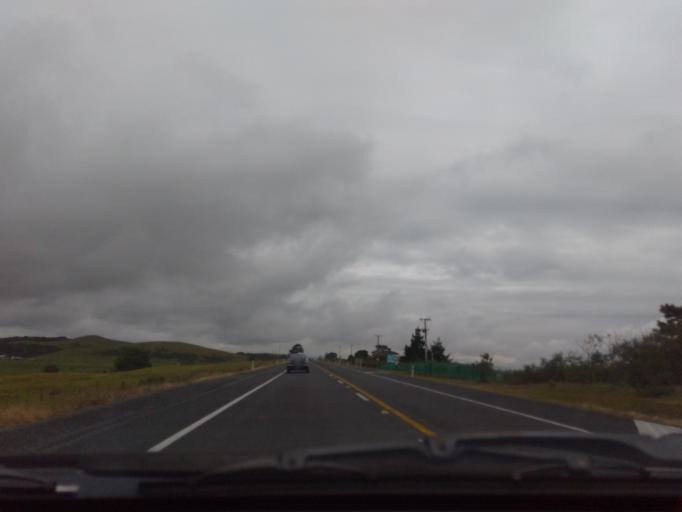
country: NZ
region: Northland
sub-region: Whangarei
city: Ruakaka
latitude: -35.9302
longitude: 174.4546
